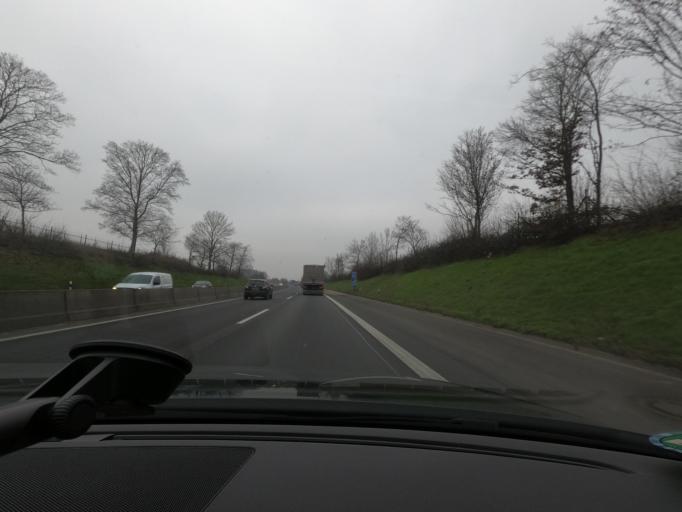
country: DE
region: North Rhine-Westphalia
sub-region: Regierungsbezirk Dusseldorf
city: Nettetal
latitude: 51.3241
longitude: 6.2208
